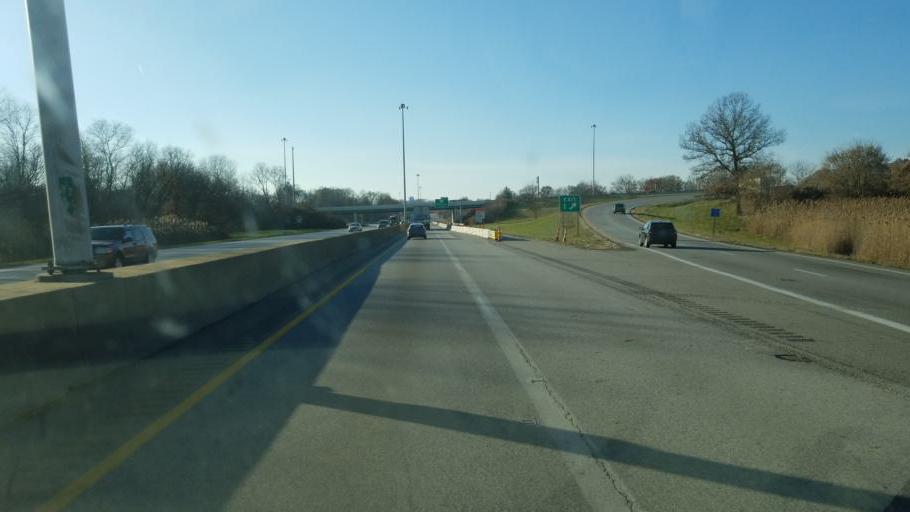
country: US
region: Ohio
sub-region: Summit County
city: Portage Lakes
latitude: 41.0355
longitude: -81.5625
